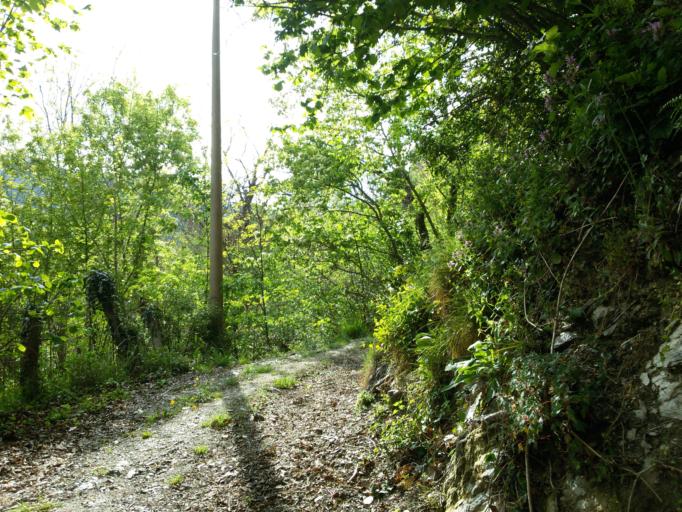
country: IT
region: Liguria
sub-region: Provincia di Genova
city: Santa Marta
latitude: 44.4775
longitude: 8.8739
